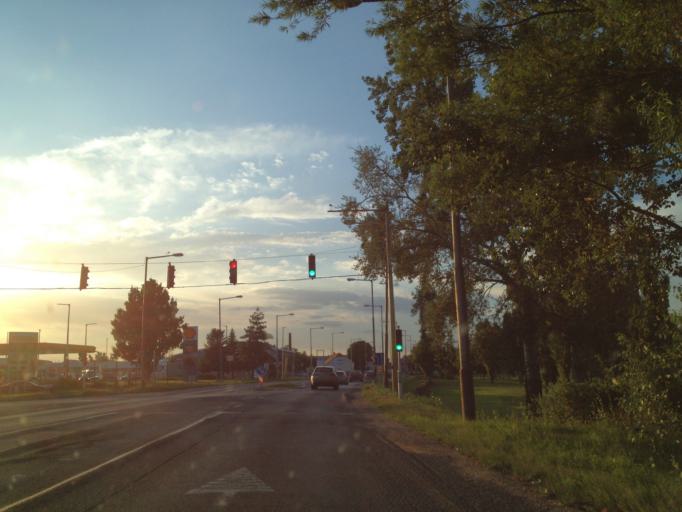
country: HU
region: Gyor-Moson-Sopron
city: Mosonmagyarovar
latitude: 47.8438
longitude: 17.2833
